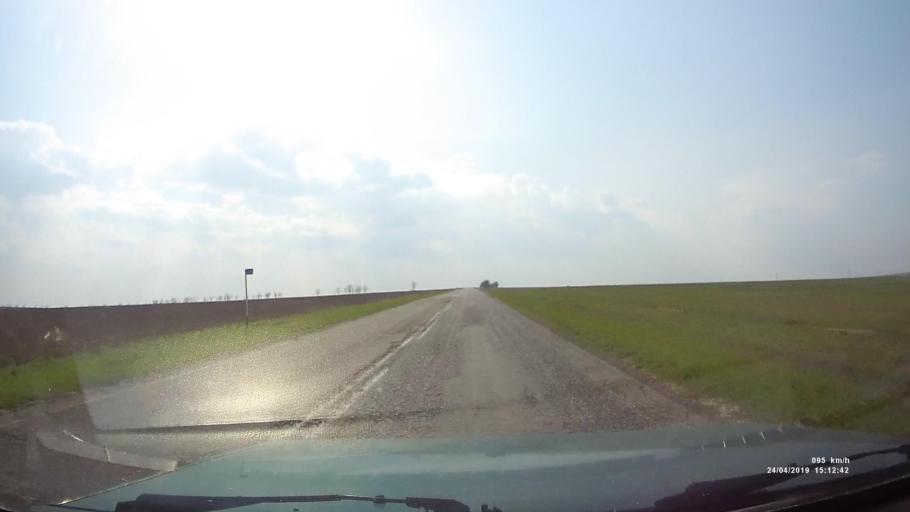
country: RU
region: Rostov
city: Remontnoye
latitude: 46.5464
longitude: 43.2949
